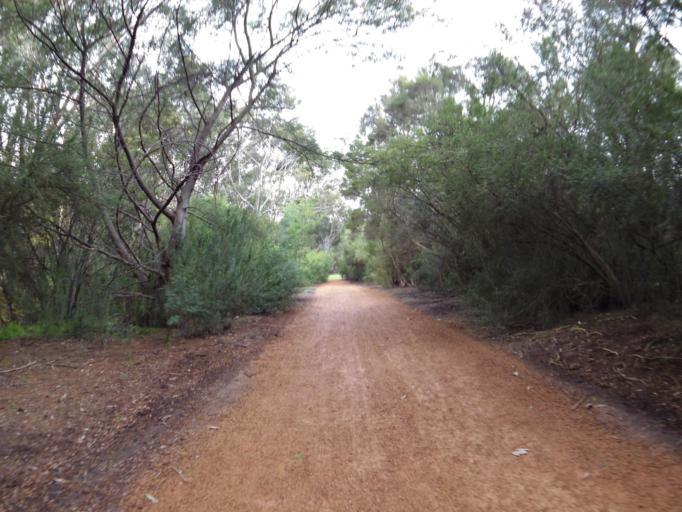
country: AU
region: Victoria
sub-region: Whitehorse
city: Mont Albert North
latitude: -37.7987
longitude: 145.1155
